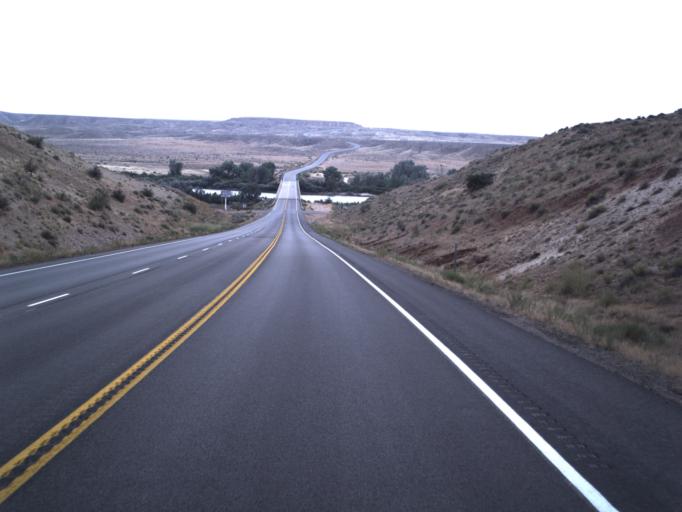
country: US
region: Utah
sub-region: Uintah County
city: Naples
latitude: 40.3198
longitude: -109.4857
